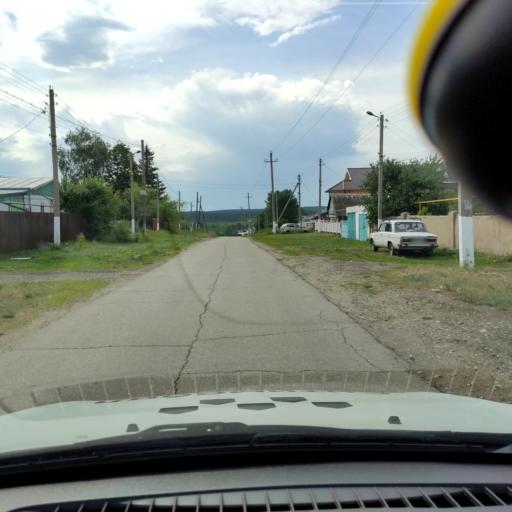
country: RU
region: Samara
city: Zhigulevsk
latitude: 53.5484
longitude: 49.5243
